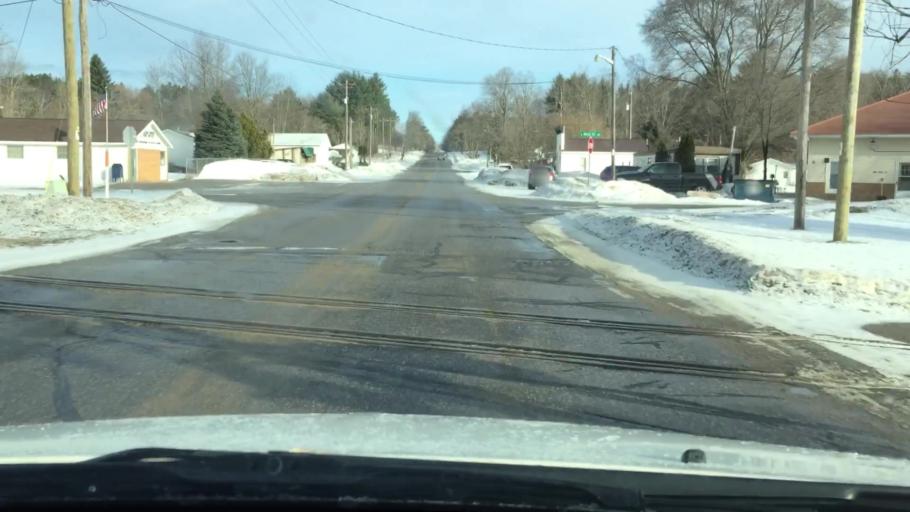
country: US
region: Michigan
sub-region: Kalkaska County
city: Kalkaska
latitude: 44.6413
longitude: -85.2802
